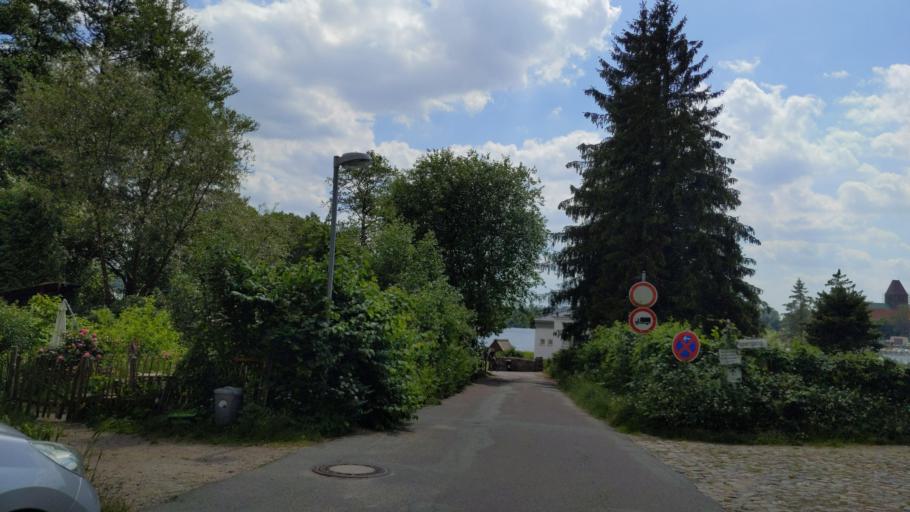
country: DE
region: Schleswig-Holstein
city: Bak
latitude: 53.7091
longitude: 10.7815
